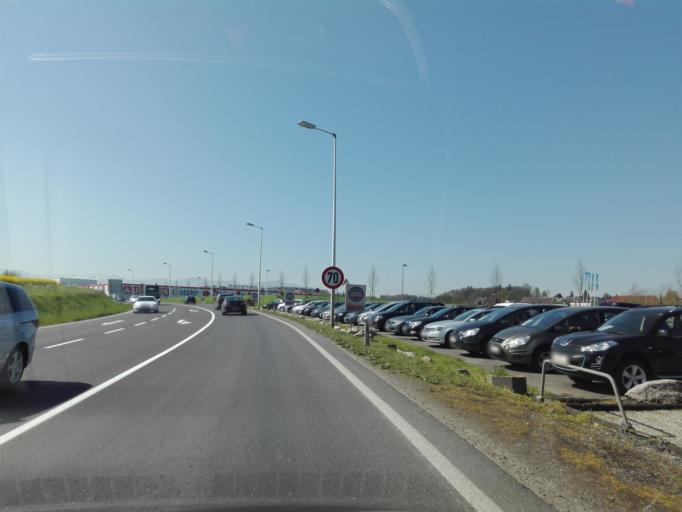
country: AT
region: Upper Austria
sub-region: Steyr Stadt
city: Steyr
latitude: 48.0669
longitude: 14.4218
